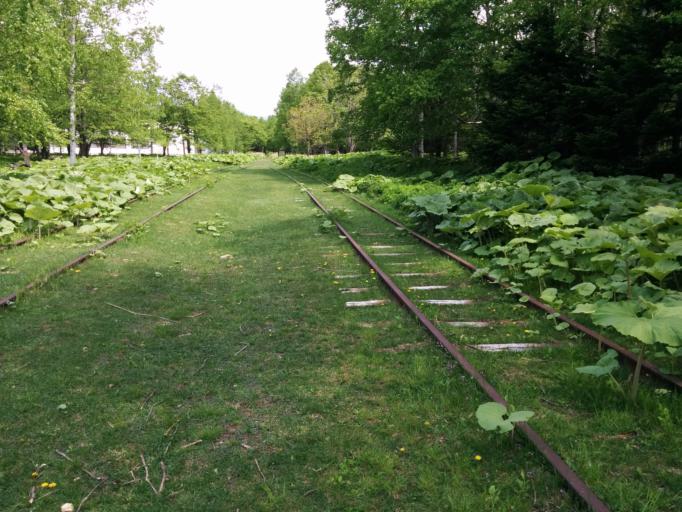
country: JP
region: Hokkaido
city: Otofuke
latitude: 43.4485
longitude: 143.1483
